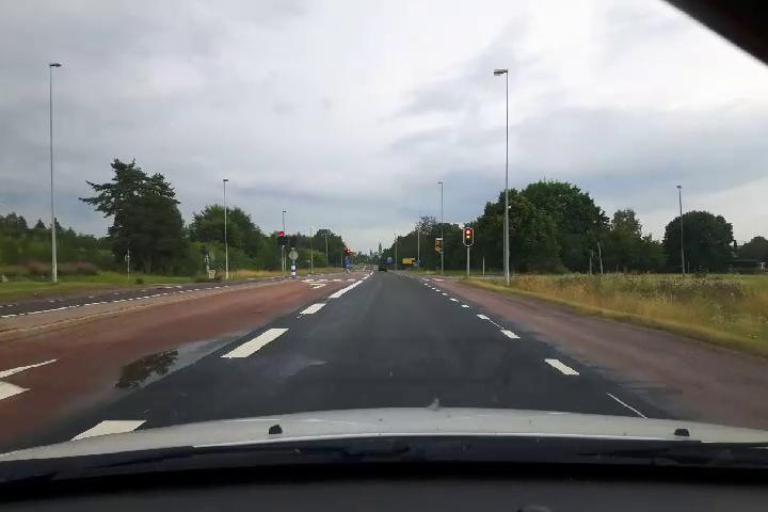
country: SE
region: Uppsala
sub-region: Uppsala Kommun
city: Gamla Uppsala
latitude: 59.8823
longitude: 17.6211
